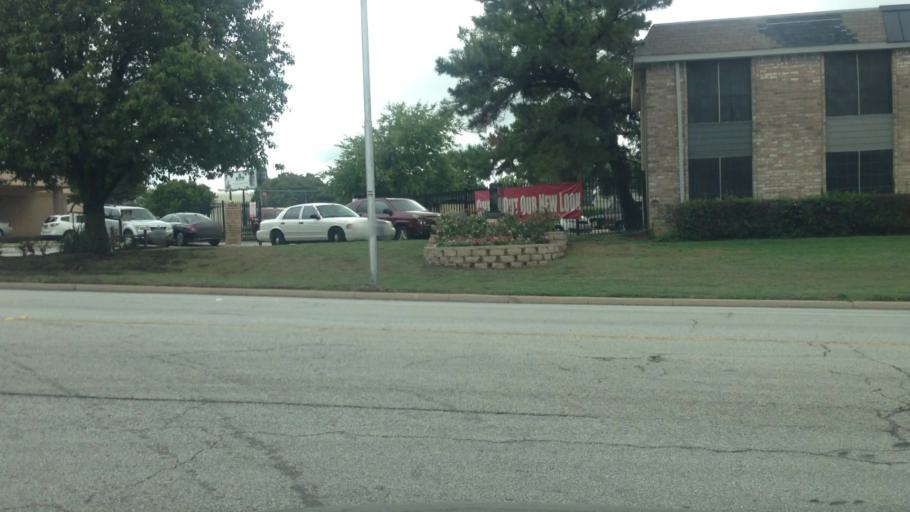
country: US
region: Texas
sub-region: Tarrant County
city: White Settlement
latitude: 32.7411
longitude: -97.4676
